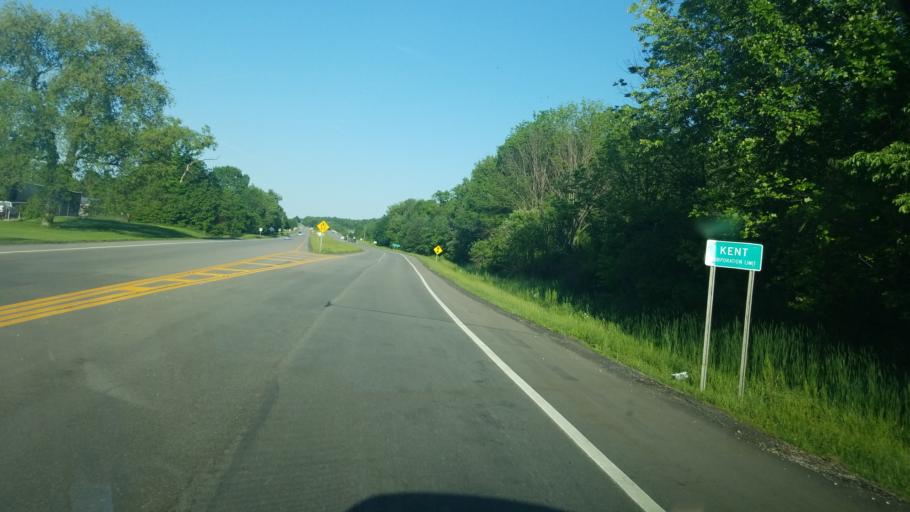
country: US
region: Ohio
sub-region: Portage County
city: Kent
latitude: 41.1352
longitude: -81.3789
